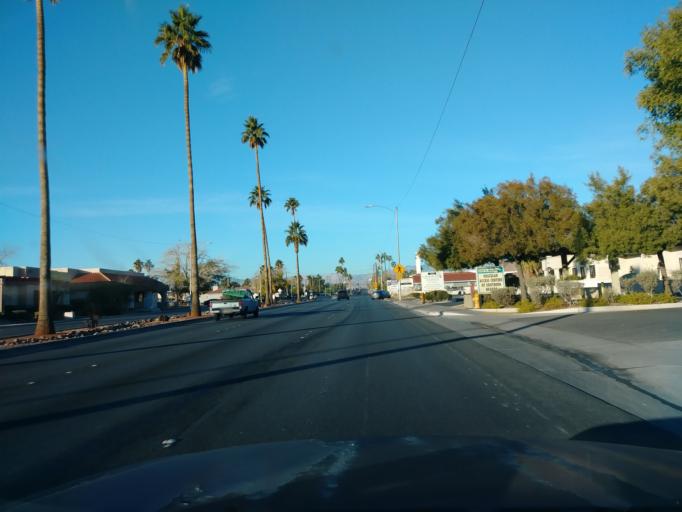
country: US
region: Nevada
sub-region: Clark County
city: Las Vegas
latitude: 36.1591
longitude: -115.1845
